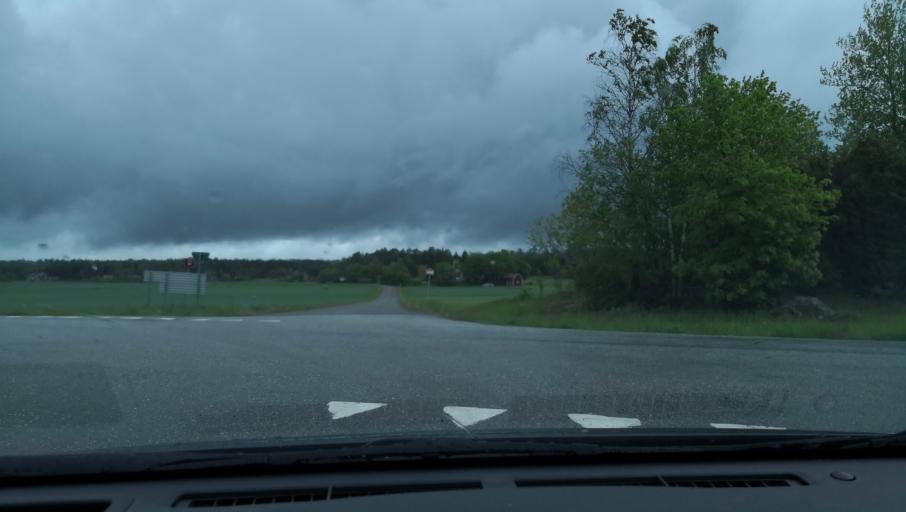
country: SE
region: Uppsala
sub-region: Enkopings Kommun
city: Orsundsbro
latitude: 59.8115
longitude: 17.3840
